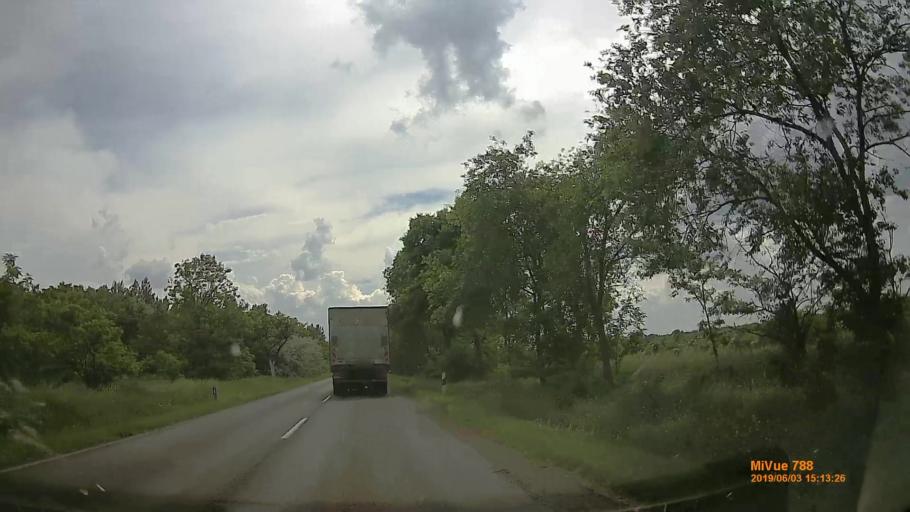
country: HU
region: Bacs-Kiskun
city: Orgovany
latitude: 46.7416
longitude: 19.5710
